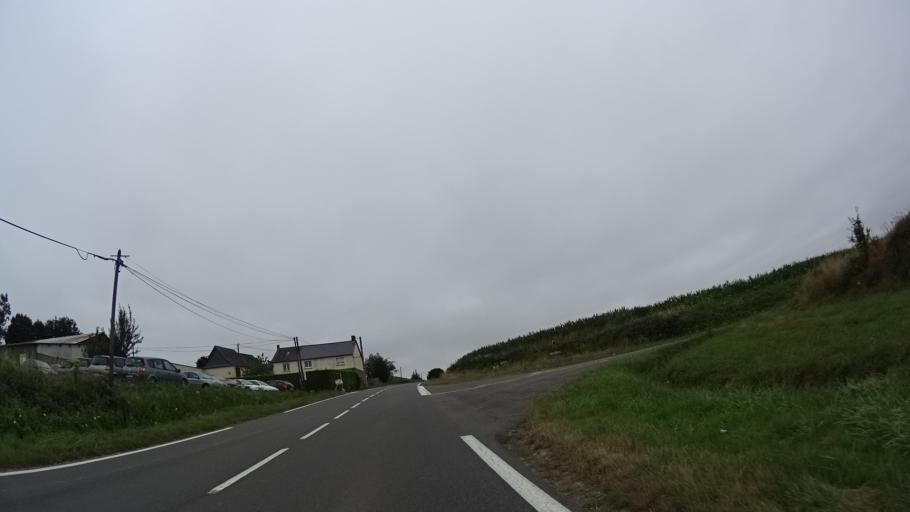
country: FR
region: Brittany
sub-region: Departement d'Ille-et-Vilaine
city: Vignoc
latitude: 48.2576
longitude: -1.8322
